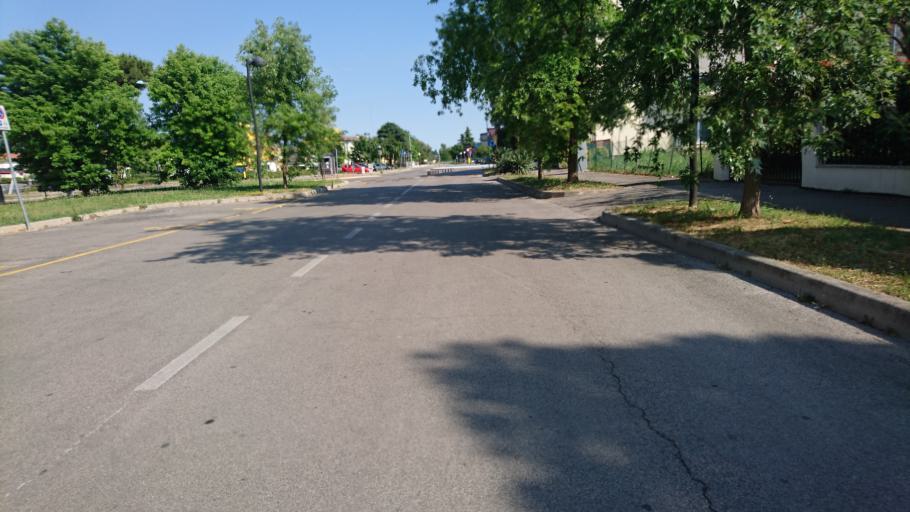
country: IT
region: Veneto
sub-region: Provincia di Padova
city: Montegrotto Terme
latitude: 45.3328
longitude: 11.7910
